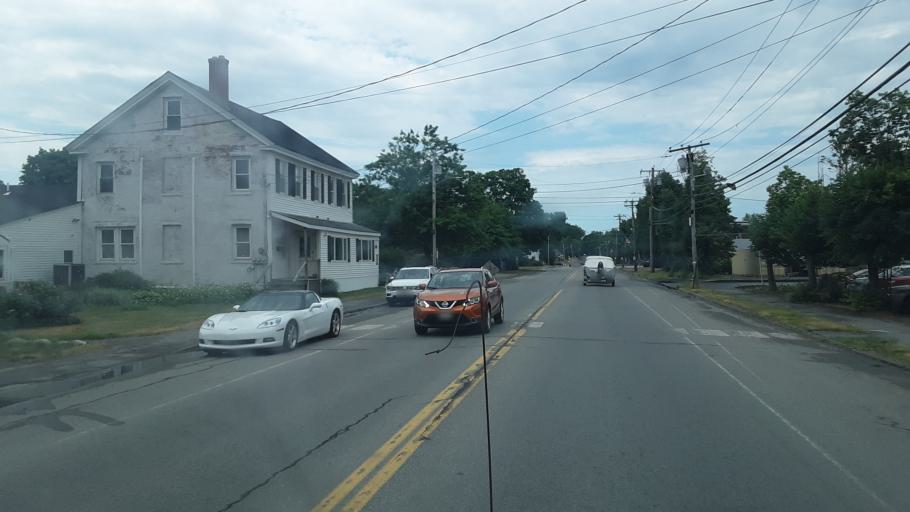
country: US
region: Maine
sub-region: Penobscot County
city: Brewer
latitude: 44.7935
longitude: -68.7670
